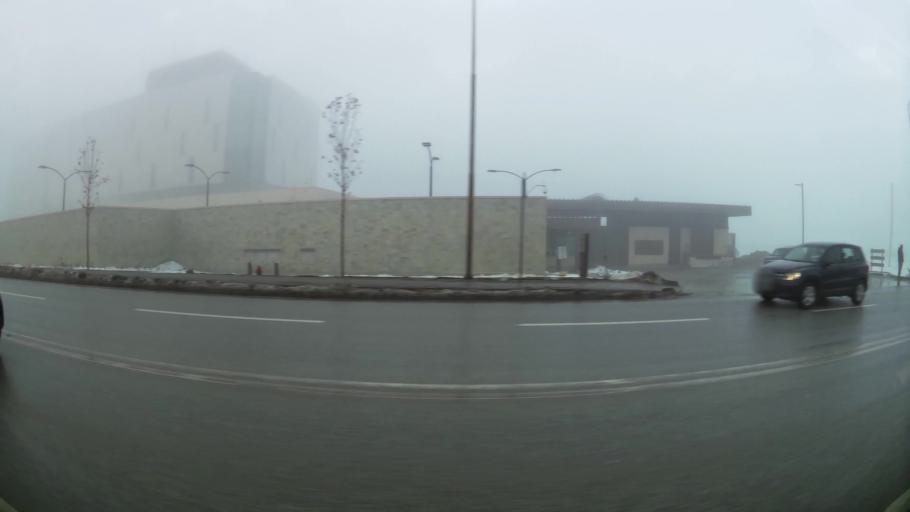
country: XK
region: Pristina
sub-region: Komuna e Prishtines
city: Pristina
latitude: 42.6574
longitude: 21.1412
